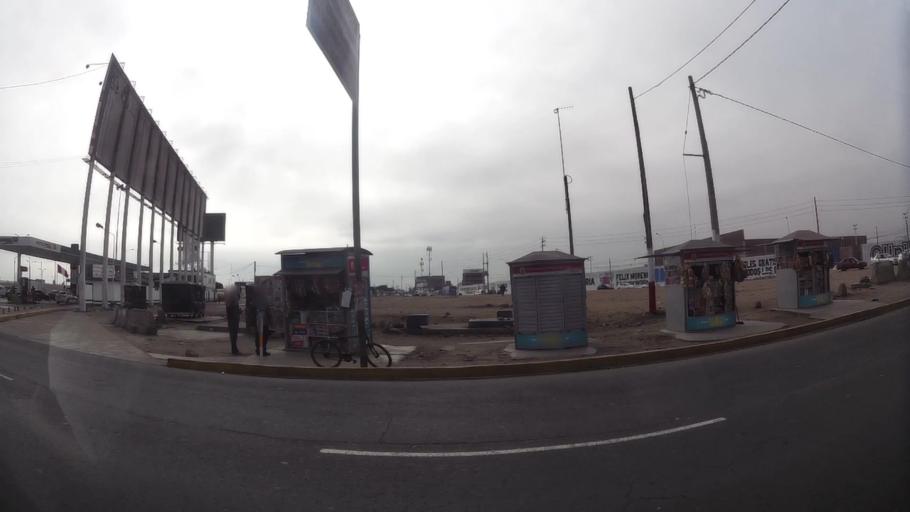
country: PE
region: Callao
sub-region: Callao
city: Callao
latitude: -12.0215
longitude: -77.1054
